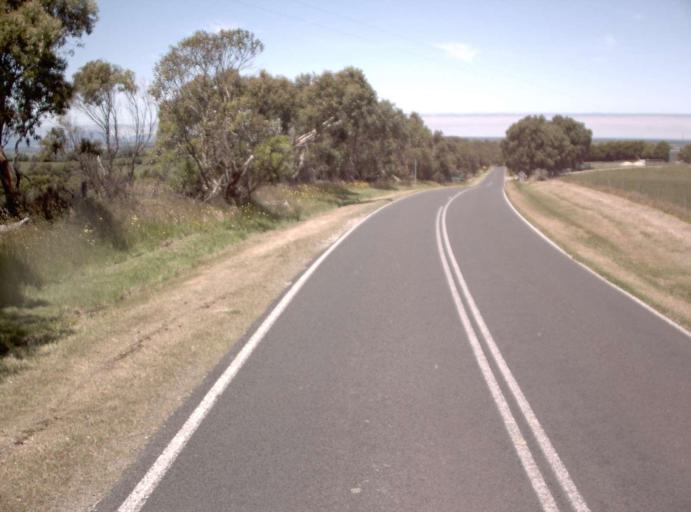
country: AU
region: Victoria
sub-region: Bass Coast
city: North Wonthaggi
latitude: -38.7470
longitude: 146.1341
